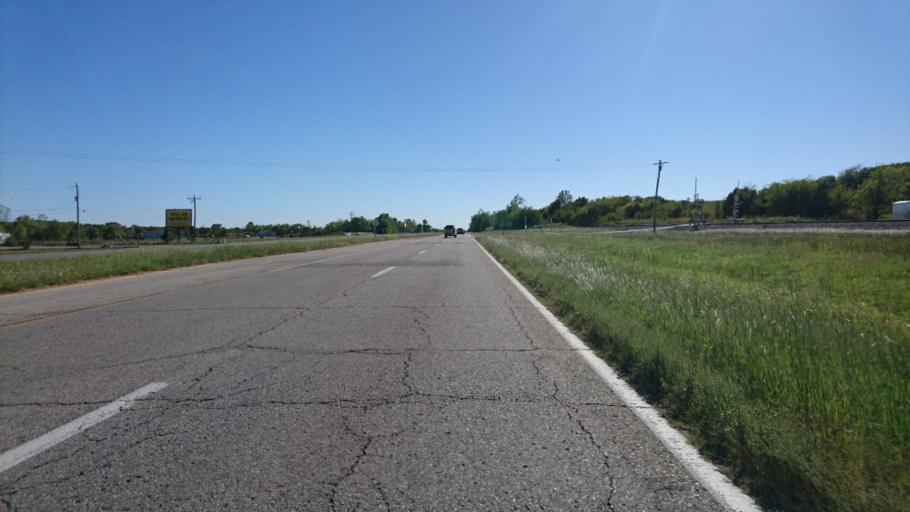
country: US
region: Oklahoma
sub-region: Rogers County
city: Bushyhead
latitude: 36.4073
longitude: -95.5411
